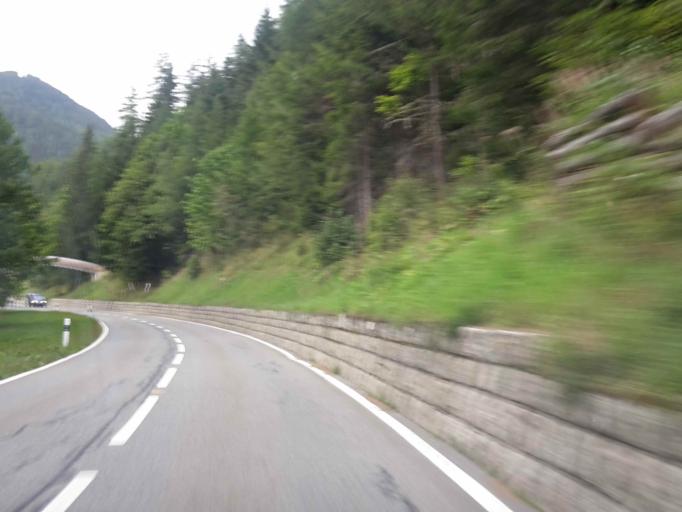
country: CH
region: Valais
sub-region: Martigny District
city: Martigny-Combe
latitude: 46.0516
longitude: 6.9994
